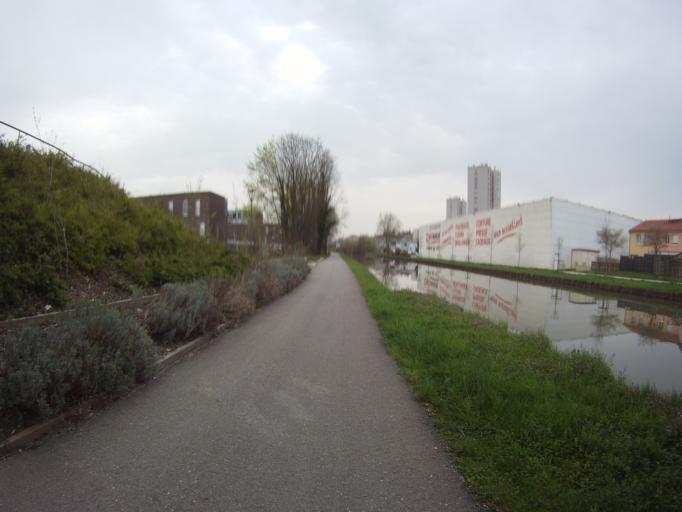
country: FR
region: Lorraine
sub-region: Departement de Meurthe-et-Moselle
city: Jarville-la-Malgrange
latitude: 48.6702
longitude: 6.2092
